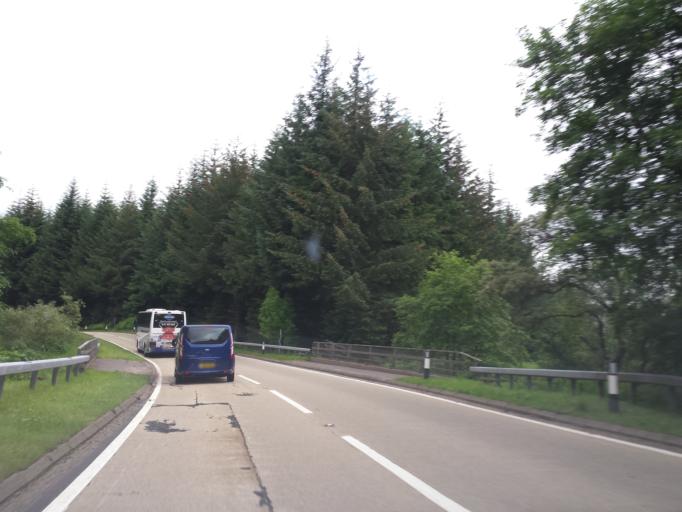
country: GB
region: Scotland
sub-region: Stirling
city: Callander
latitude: 56.4367
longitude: -4.3437
